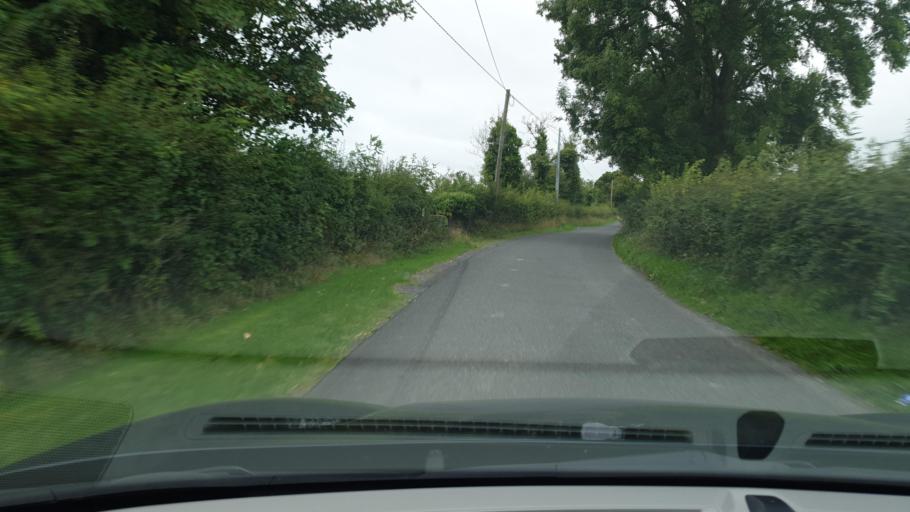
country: IE
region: Leinster
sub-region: An Mhi
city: Ratoath
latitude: 53.5243
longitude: -6.4920
